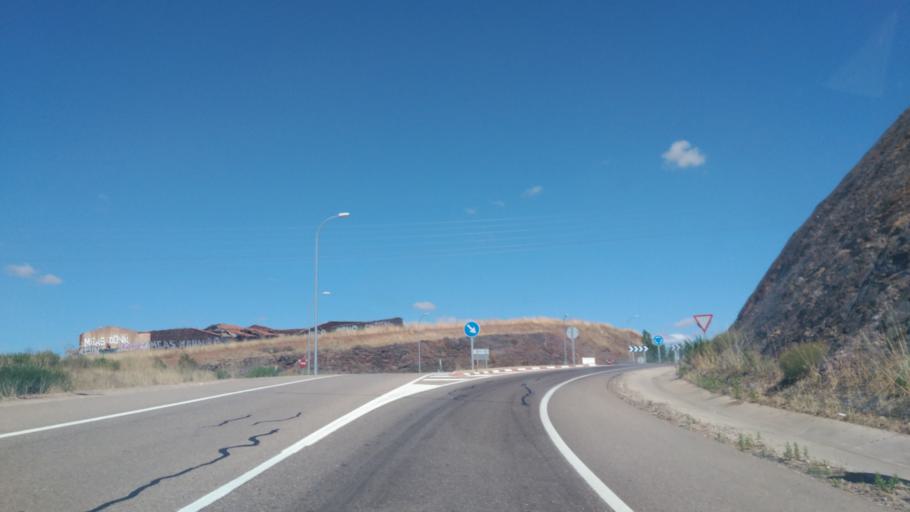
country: ES
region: Castille and Leon
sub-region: Provincia de Salamanca
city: Villamayor
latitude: 40.9627
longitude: -5.7025
